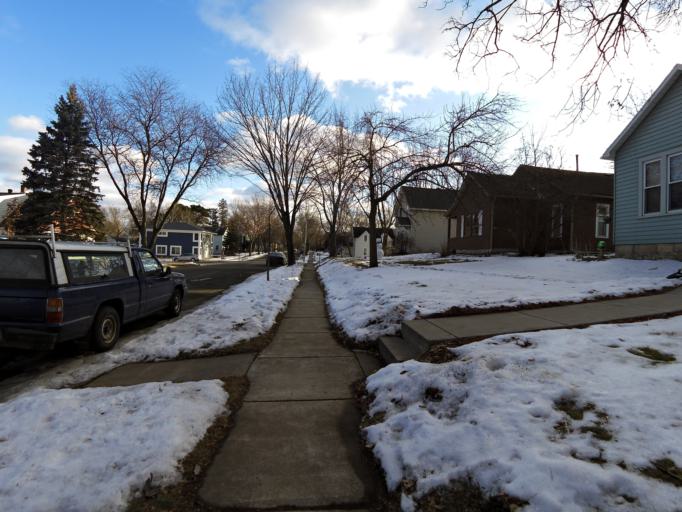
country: US
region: Minnesota
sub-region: Washington County
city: Bayport
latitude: 45.0200
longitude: -92.7826
